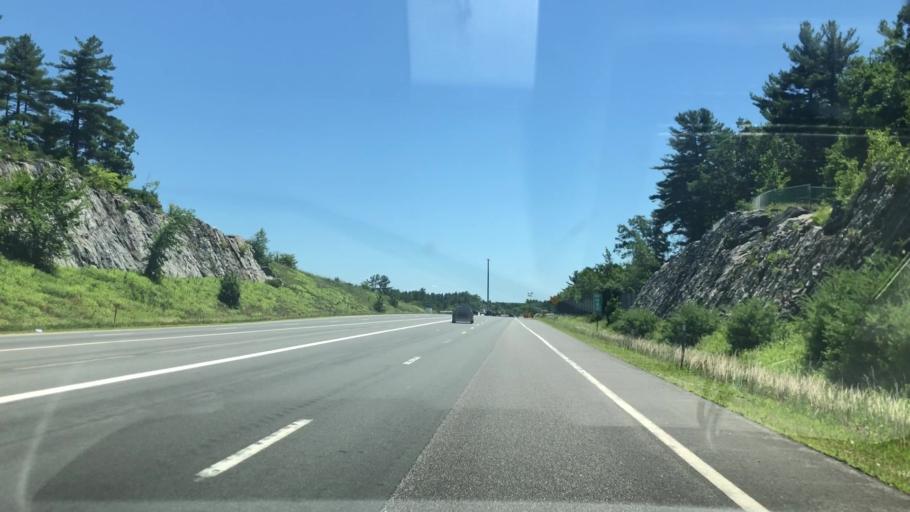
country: US
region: New Hampshire
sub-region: Hillsborough County
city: Manchester
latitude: 42.9566
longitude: -71.4069
